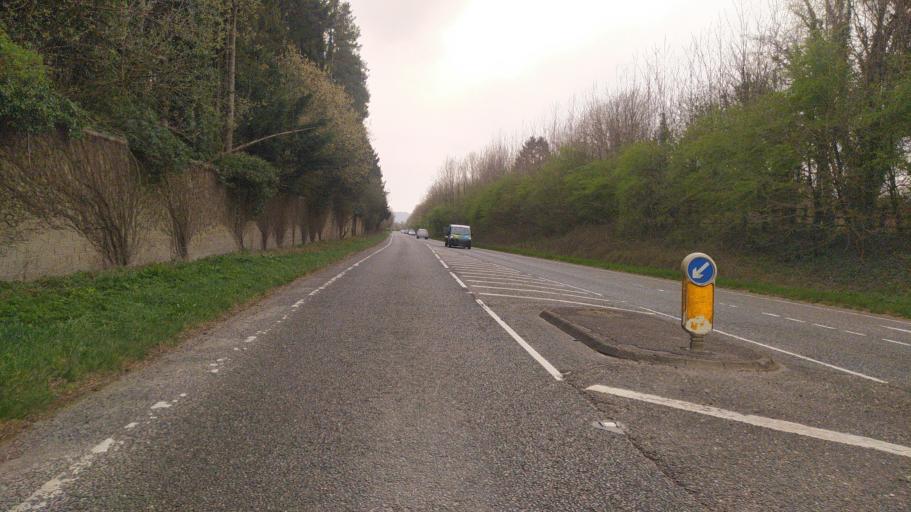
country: GB
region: England
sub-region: Wiltshire
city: Hindon
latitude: 51.0759
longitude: -2.1680
